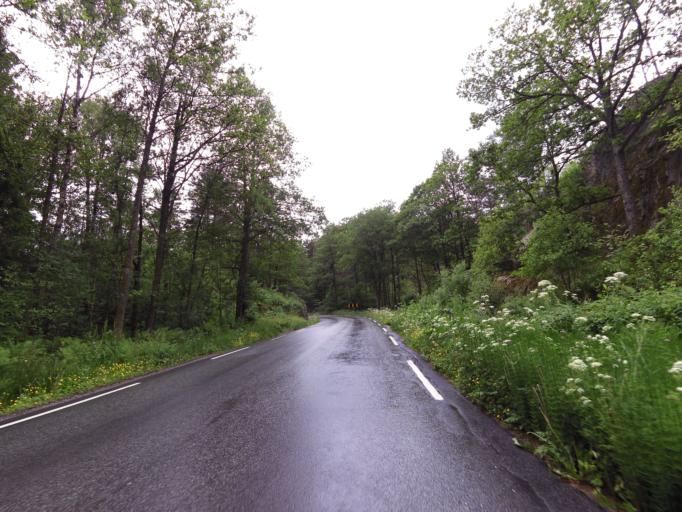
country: NO
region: Vest-Agder
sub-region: Mandal
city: Mandal
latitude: 58.0161
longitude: 7.5119
